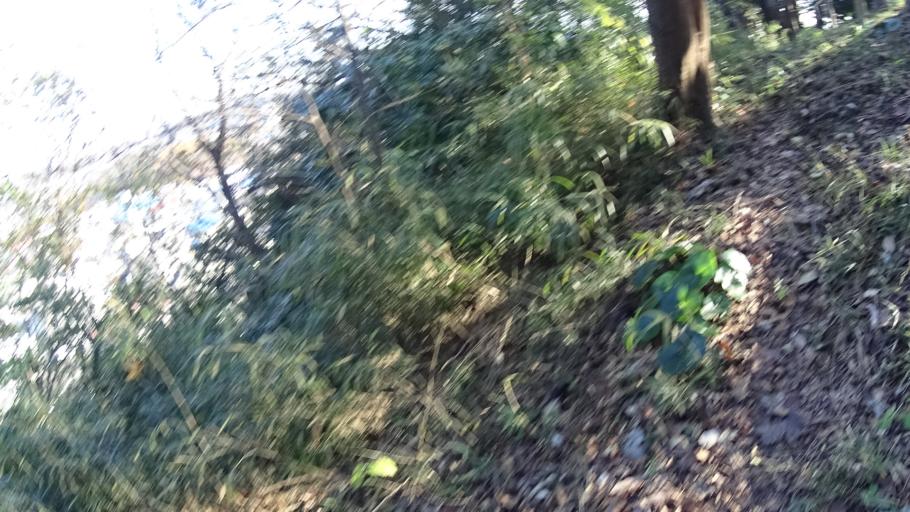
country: JP
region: Kanagawa
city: Zushi
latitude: 35.2874
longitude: 139.5846
